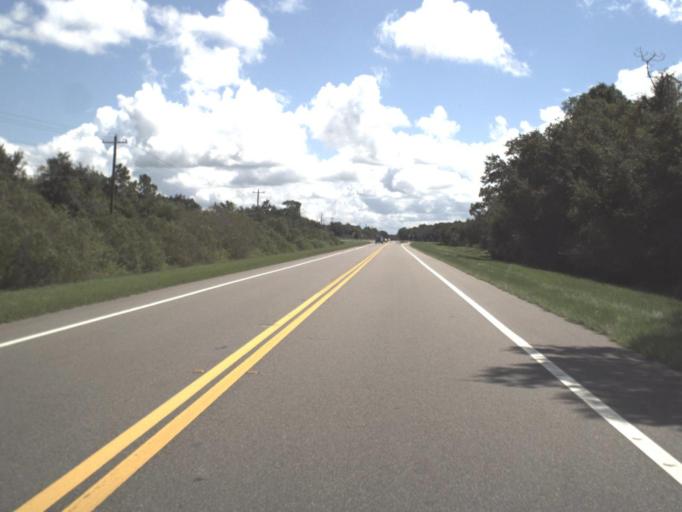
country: US
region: Florida
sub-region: Sarasota County
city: The Meadows
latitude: 27.4009
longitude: -82.3086
